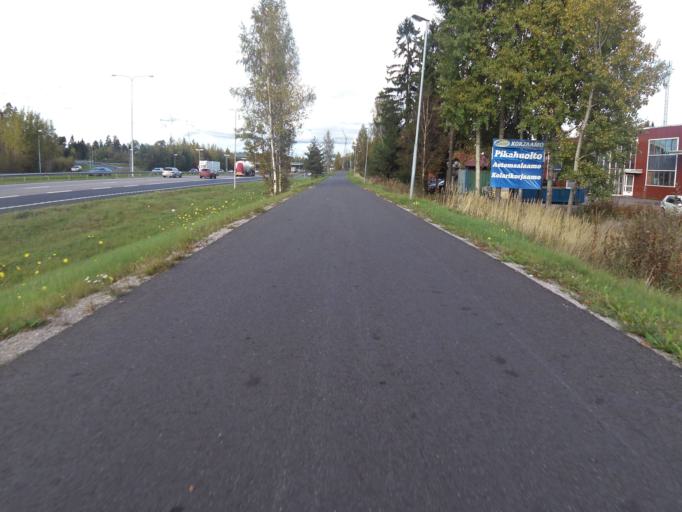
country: FI
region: Uusimaa
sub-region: Helsinki
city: Kauniainen
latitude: 60.2379
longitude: 24.6949
